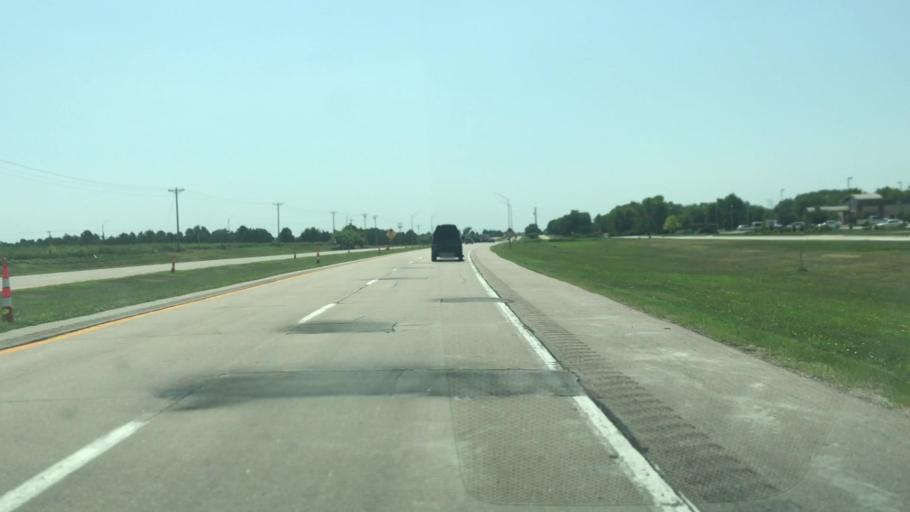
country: US
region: Nebraska
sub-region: Adams County
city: Hastings
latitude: 40.6434
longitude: -98.3821
